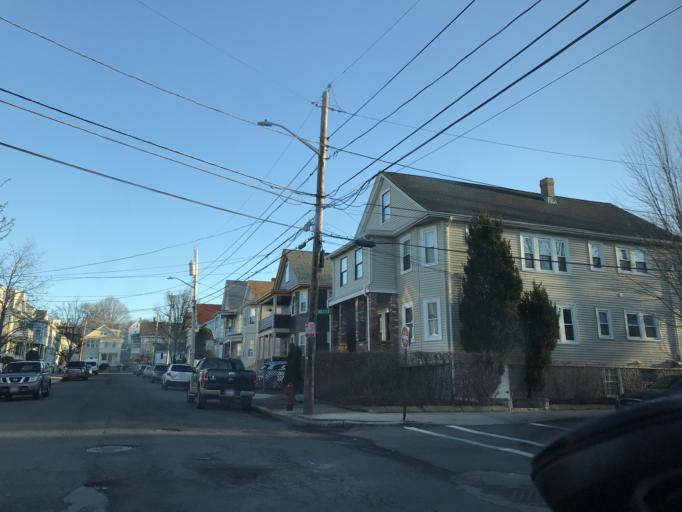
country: US
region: Massachusetts
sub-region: Middlesex County
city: Everett
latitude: 42.4193
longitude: -71.0486
